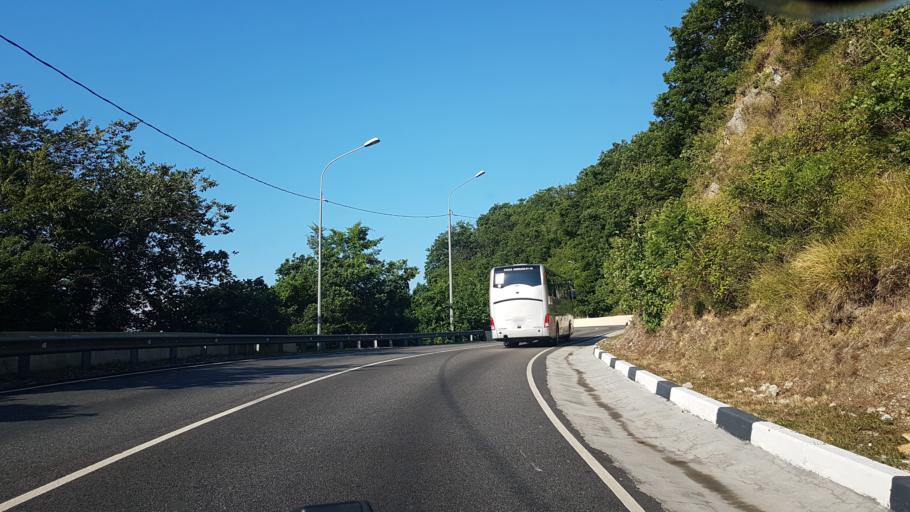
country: RU
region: Krasnodarskiy
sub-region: Sochi City
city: Lazarevskoye
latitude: 43.8531
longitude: 39.4087
